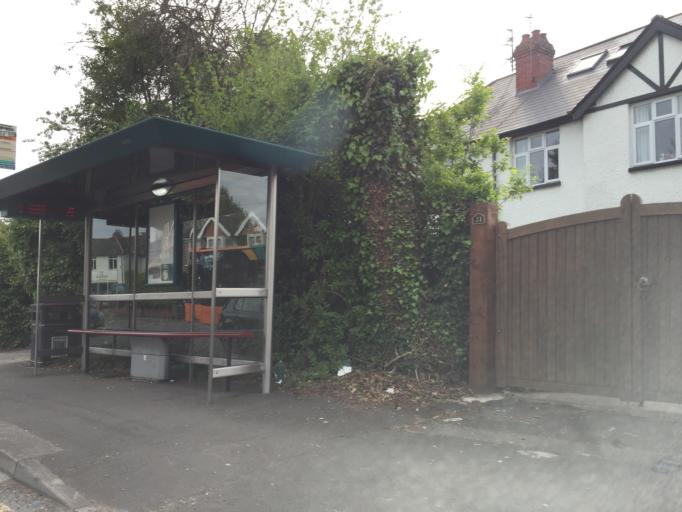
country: GB
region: Wales
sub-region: Caerphilly County Borough
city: Caerphilly
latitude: 51.5262
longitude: -3.2029
